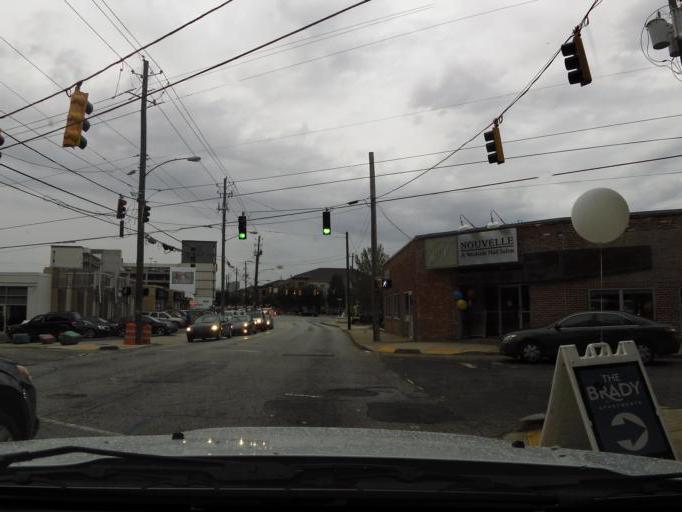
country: US
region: Georgia
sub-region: Fulton County
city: Atlanta
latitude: 33.7798
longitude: -84.4103
